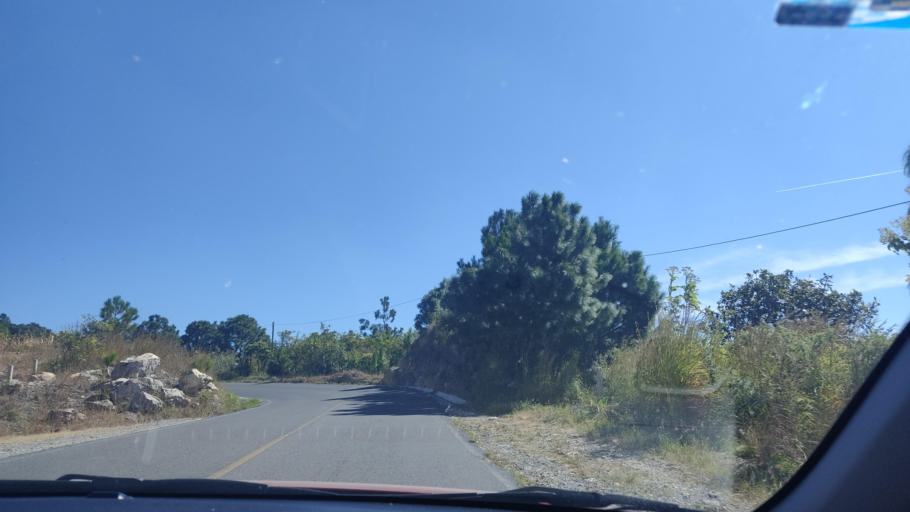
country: MX
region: Nayarit
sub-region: Jala
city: Rosa Blanca
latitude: 21.1001
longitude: -104.3693
